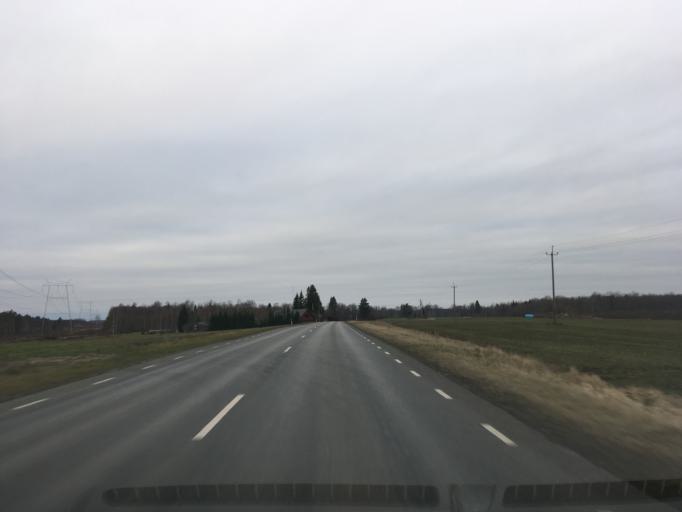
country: EE
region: Laeaene
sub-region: Lihula vald
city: Lihula
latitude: 58.5216
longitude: 24.0756
